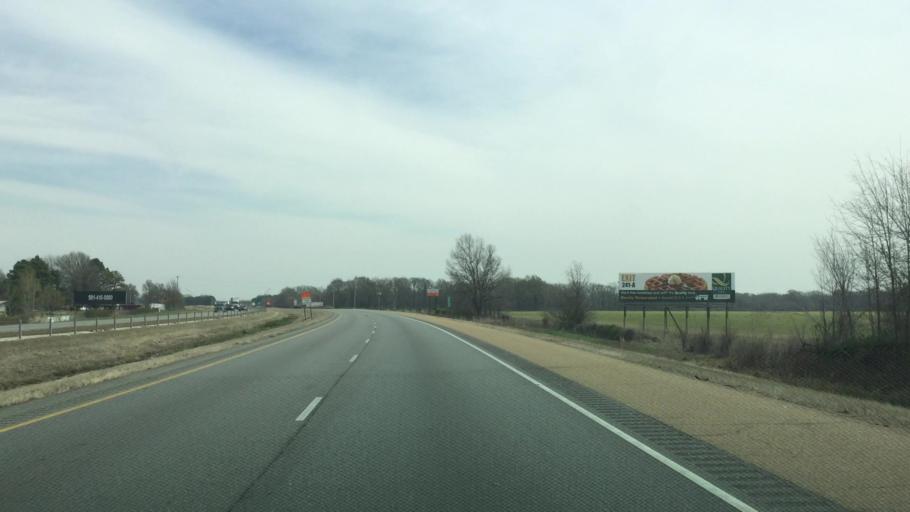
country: US
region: Arkansas
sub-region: Saint Francis County
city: Forrest City
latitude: 34.9771
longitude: -90.9211
